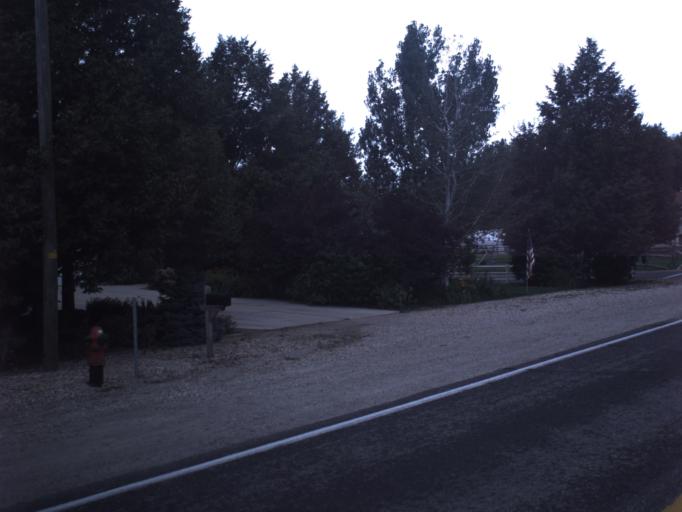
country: US
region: Utah
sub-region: Davis County
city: West Point
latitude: 41.0921
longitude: -112.1128
